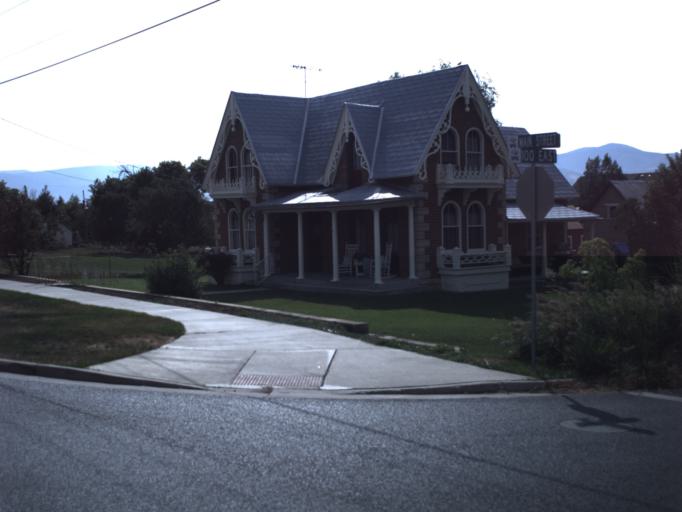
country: US
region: Utah
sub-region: Wasatch County
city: Midway
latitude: 40.5121
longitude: -111.4702
